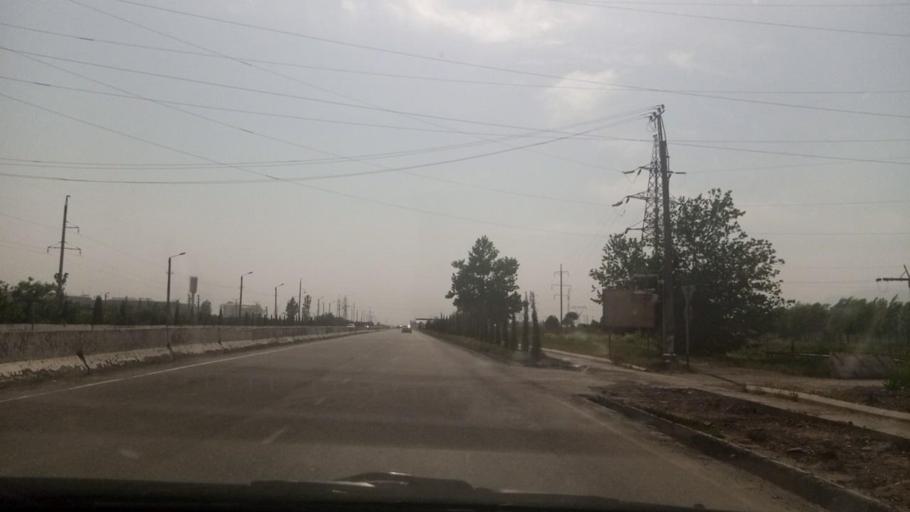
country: UZ
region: Toshkent
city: Angren
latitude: 41.0206
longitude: 70.1211
